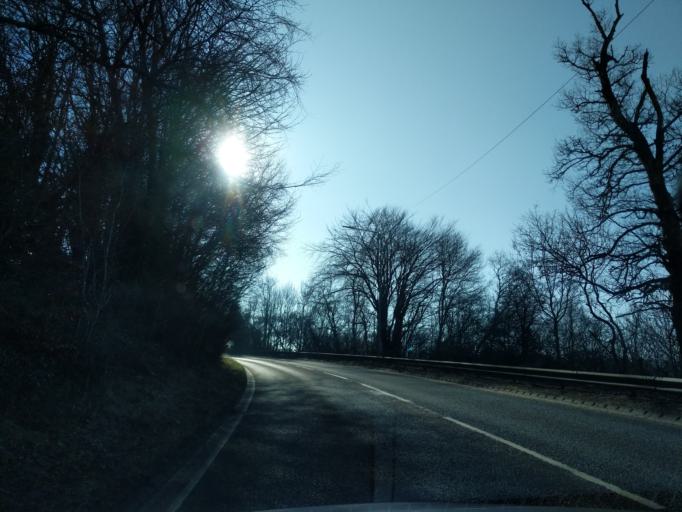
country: GB
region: Scotland
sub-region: South Lanarkshire
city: Lanark
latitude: 55.6781
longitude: -3.7965
